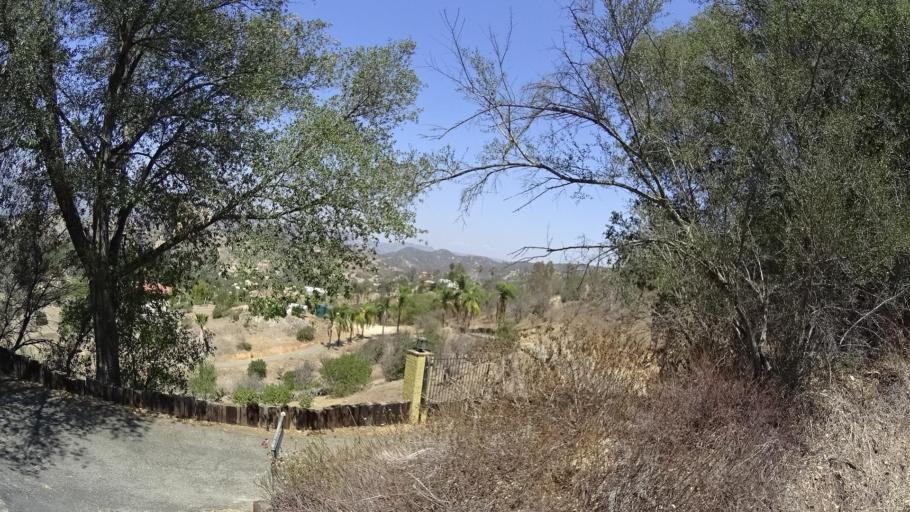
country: US
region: California
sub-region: San Diego County
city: Fallbrook
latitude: 33.4333
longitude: -117.2914
